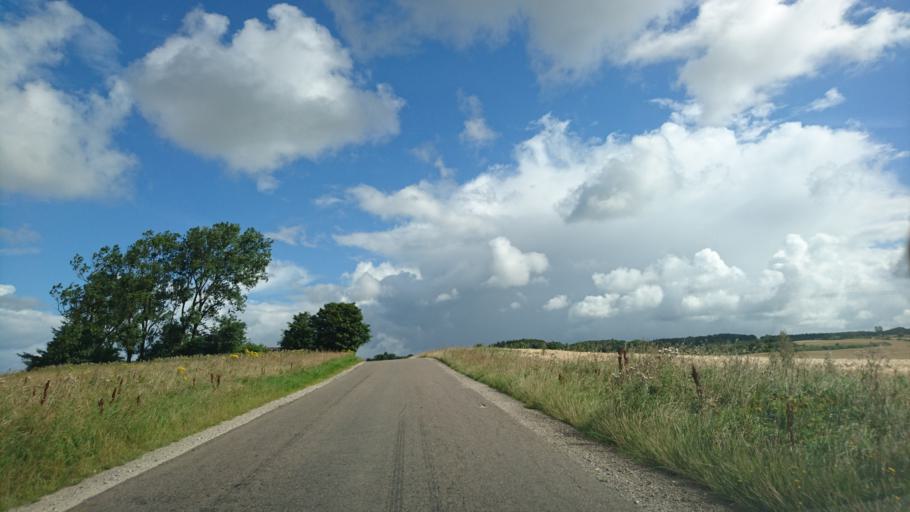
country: DK
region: North Denmark
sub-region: Hjorring Kommune
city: Tars
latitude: 57.3888
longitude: 10.1890
